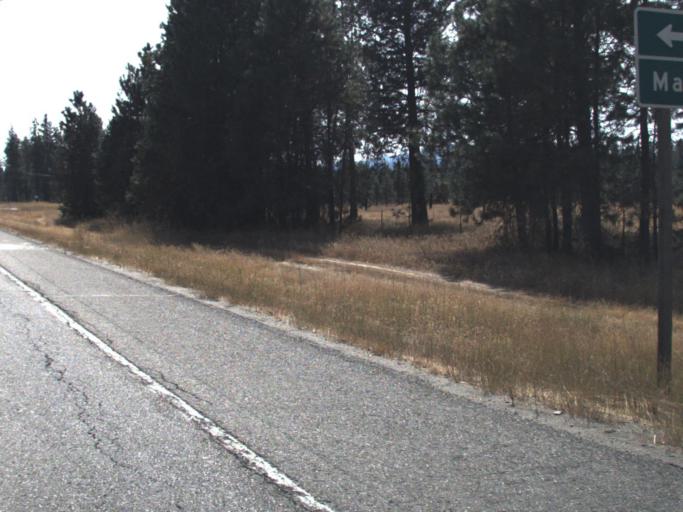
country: US
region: Washington
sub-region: Spokane County
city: Deer Park
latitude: 48.0821
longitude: -117.6310
